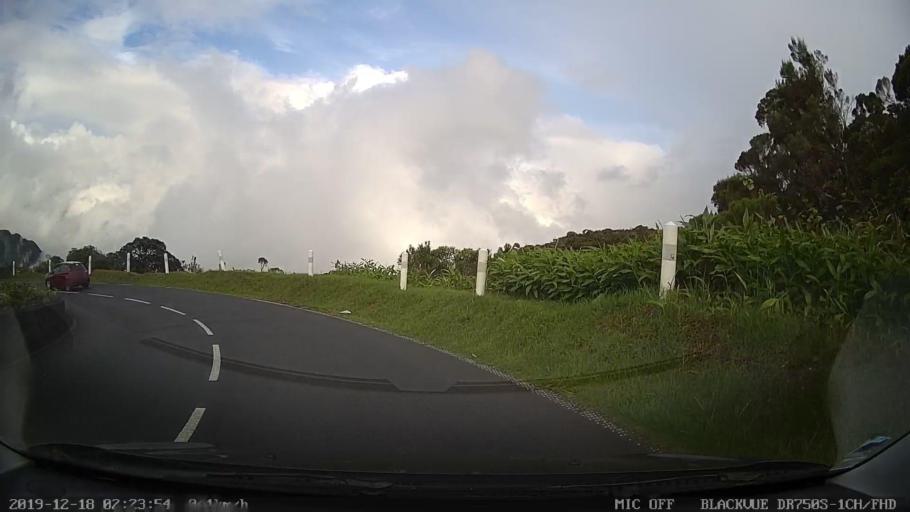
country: RE
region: Reunion
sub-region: Reunion
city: Cilaos
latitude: -21.1643
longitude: 55.5910
